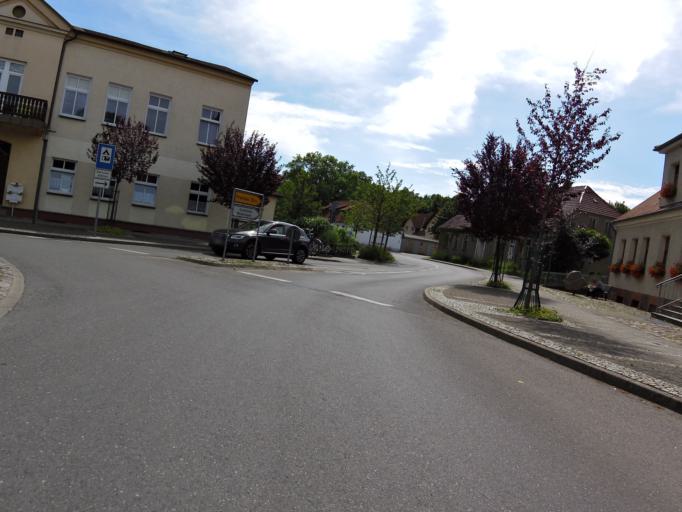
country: DE
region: Mecklenburg-Vorpommern
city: Loitz
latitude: 53.3355
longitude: 13.4399
